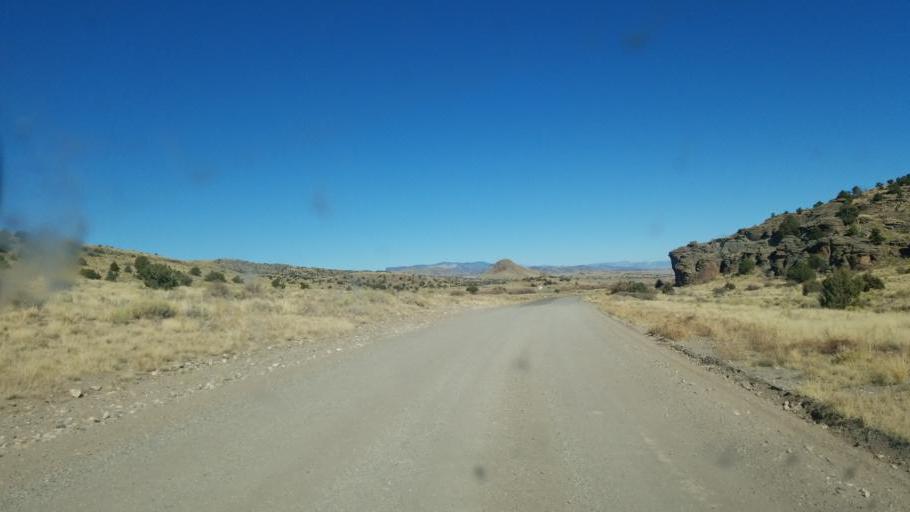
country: US
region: Colorado
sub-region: Rio Grande County
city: Del Norte
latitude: 37.6375
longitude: -106.3660
